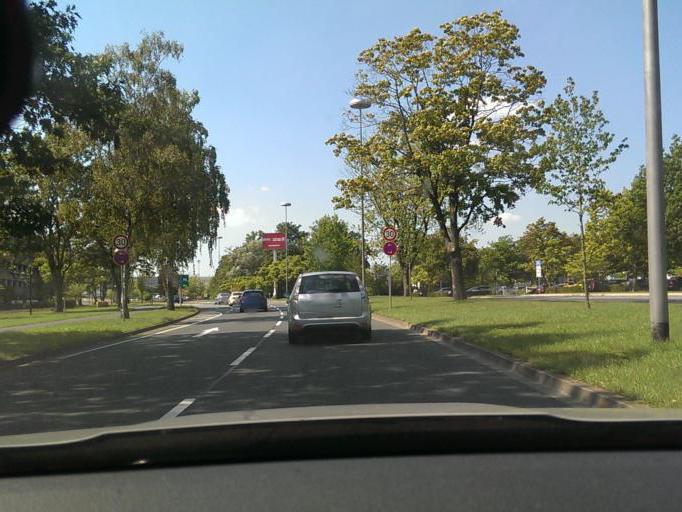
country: DE
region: Lower Saxony
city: Langenhagen
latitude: 52.4616
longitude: 9.6983
